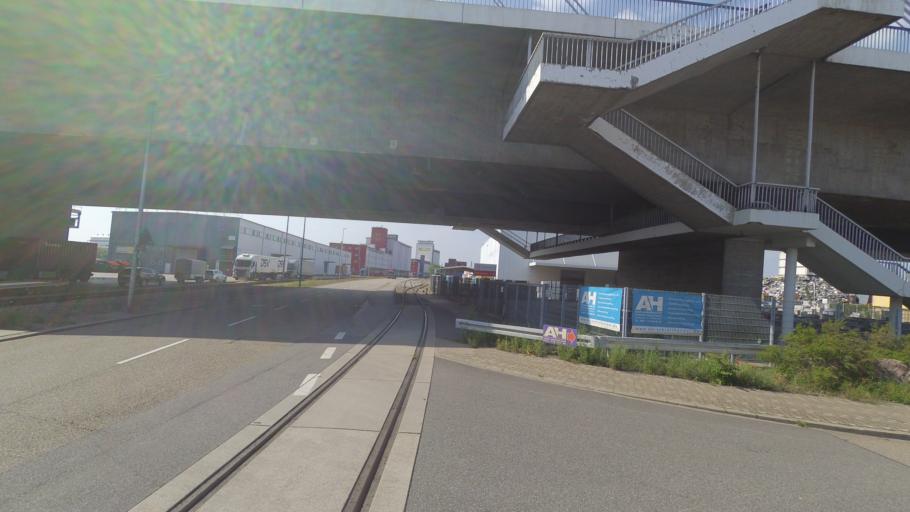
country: DE
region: Rheinland-Pfalz
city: Ludwigshafen am Rhein
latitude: 49.4902
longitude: 8.4480
